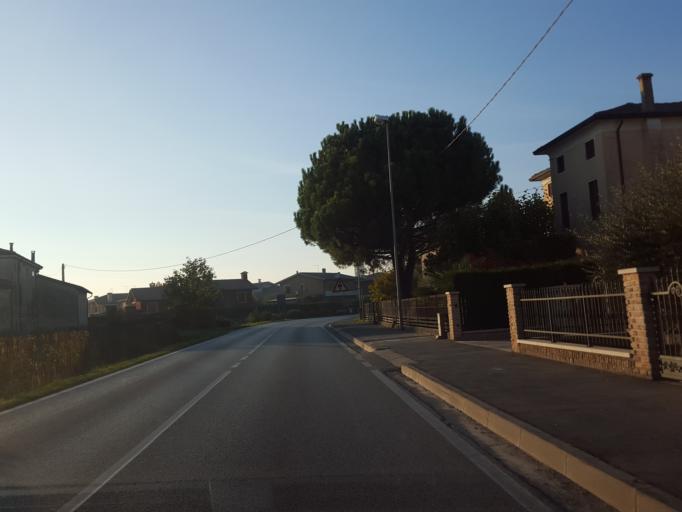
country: IT
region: Veneto
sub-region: Provincia di Vicenza
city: Camisano Vicentino
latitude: 45.5211
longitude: 11.7210
